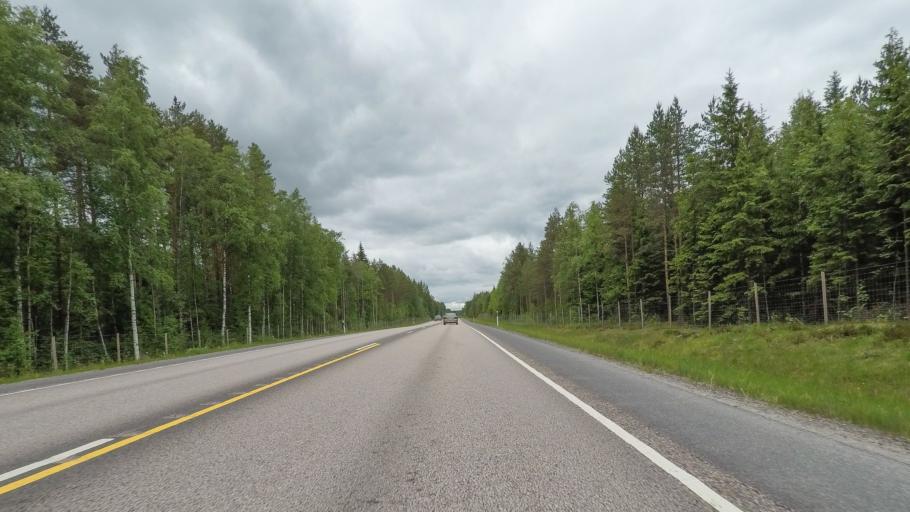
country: FI
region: Central Finland
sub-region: Joutsa
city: Leivonmaeki
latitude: 61.8340
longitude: 26.0966
